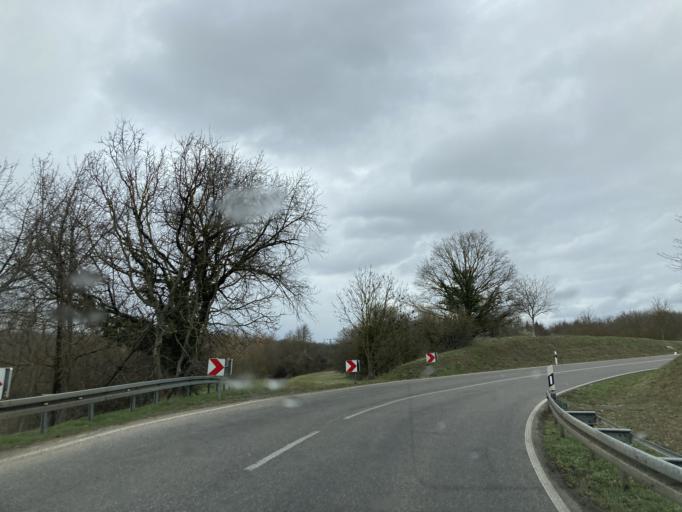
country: DE
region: Baden-Wuerttemberg
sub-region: Freiburg Region
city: Hartheim
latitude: 47.8951
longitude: 7.5970
